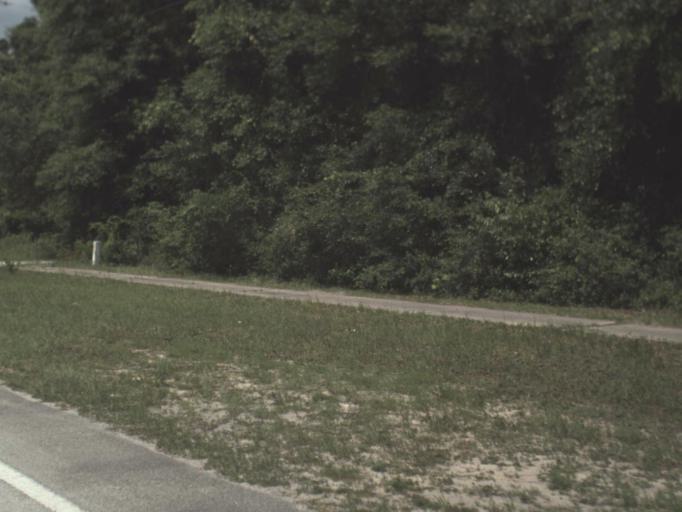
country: US
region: Florida
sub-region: Bradford County
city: Starke
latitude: 29.9613
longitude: -82.0163
